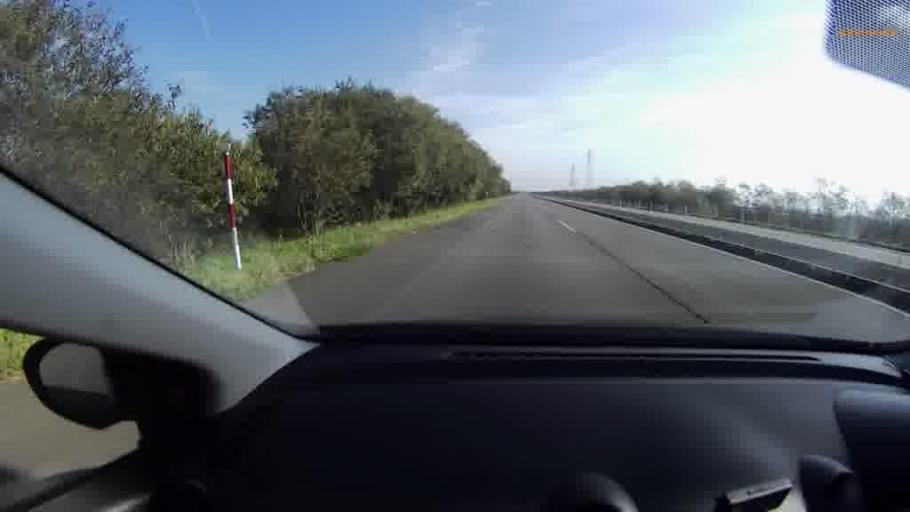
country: JP
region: Hokkaido
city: Kushiro
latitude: 43.0271
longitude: 144.2914
